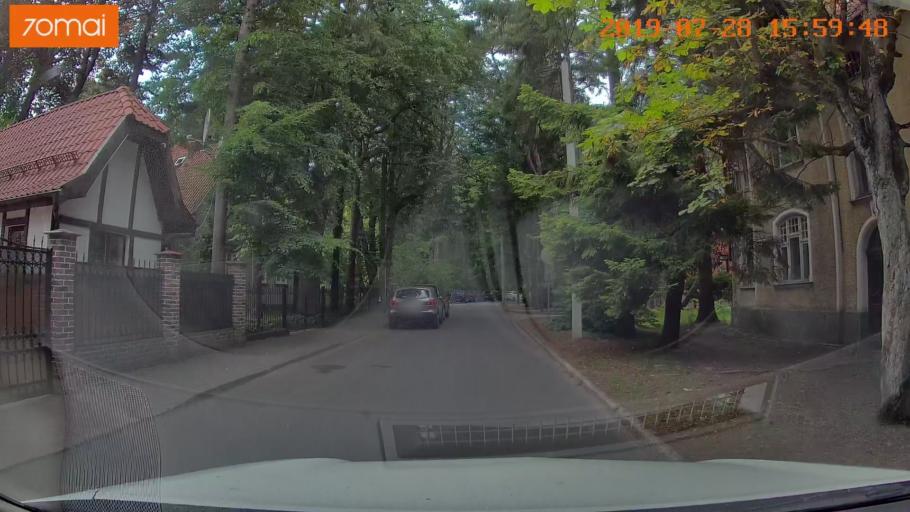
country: RU
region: Kaliningrad
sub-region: Gorod Svetlogorsk
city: Svetlogorsk
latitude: 54.9424
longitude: 20.1582
